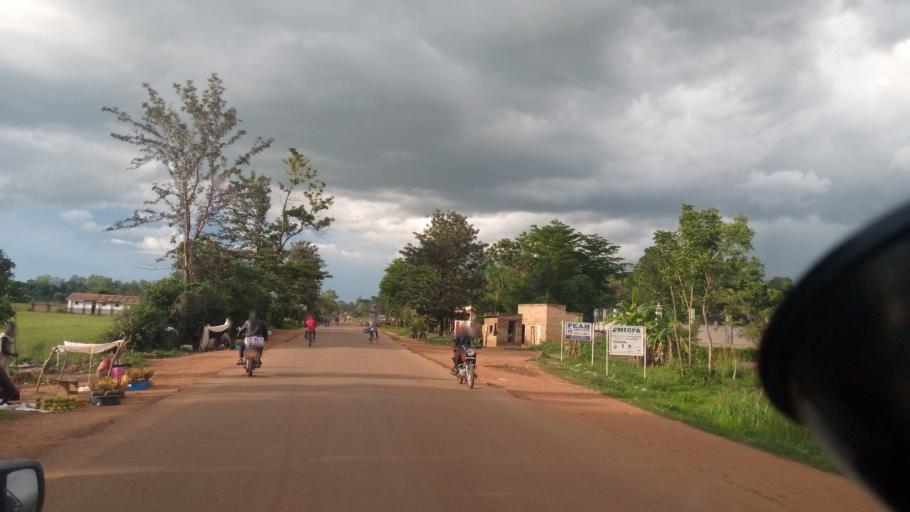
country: UG
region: Northern Region
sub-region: Lira District
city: Lira
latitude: 2.2678
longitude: 32.9133
